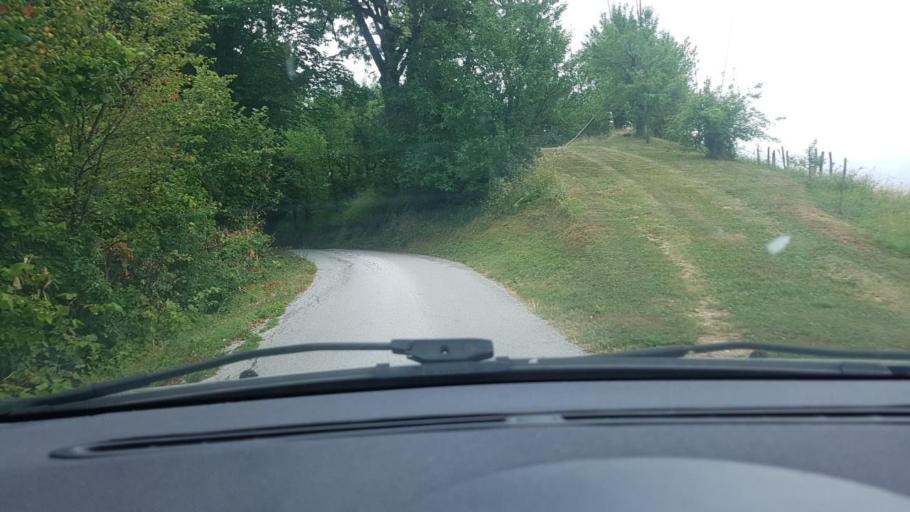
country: SI
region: Videm
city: Videm pri Ptuju
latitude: 46.3367
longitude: 15.9140
